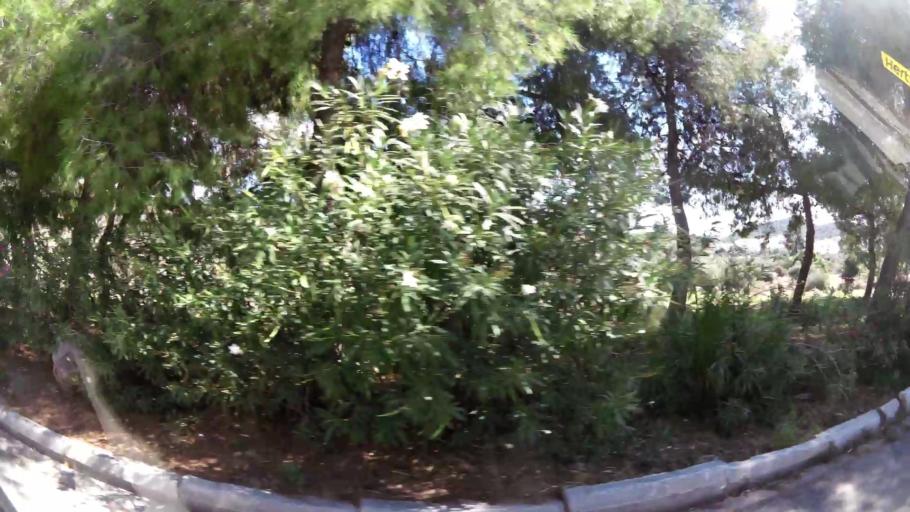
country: GR
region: Attica
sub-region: Nomarchia Anatolikis Attikis
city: Voula
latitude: 37.8414
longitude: 23.7845
